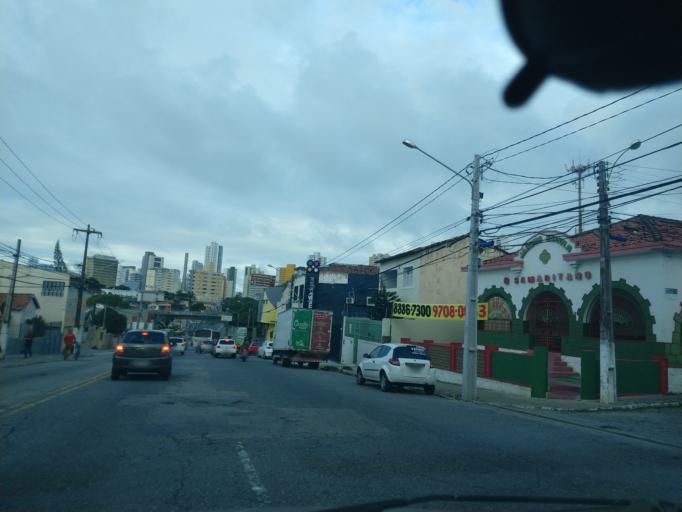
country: BR
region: Rio Grande do Norte
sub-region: Natal
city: Natal
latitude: -5.7919
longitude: -35.2108
